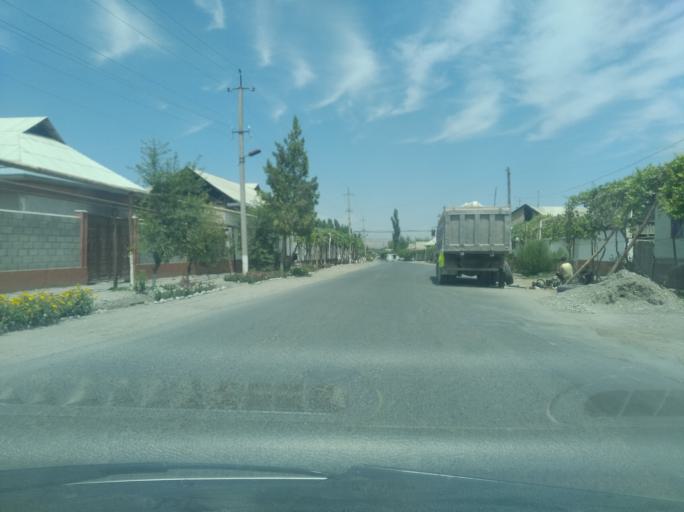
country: KG
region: Osh
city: Aravan
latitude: 40.6159
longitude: 72.4548
